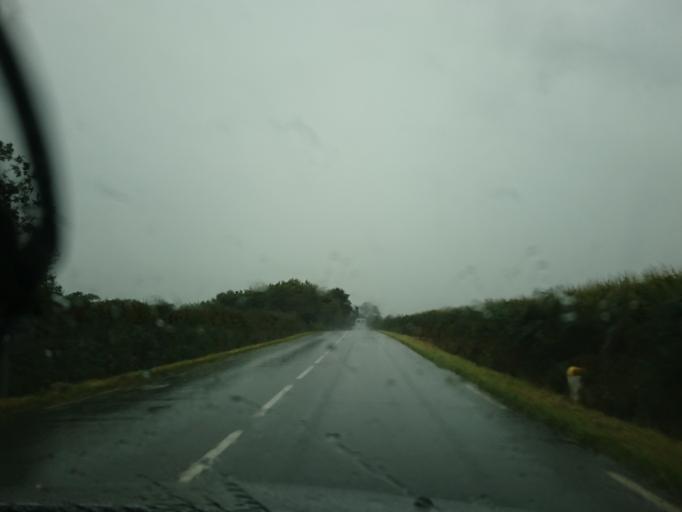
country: FR
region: Brittany
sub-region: Departement du Finistere
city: Le Drennec
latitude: 48.5244
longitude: -4.3886
